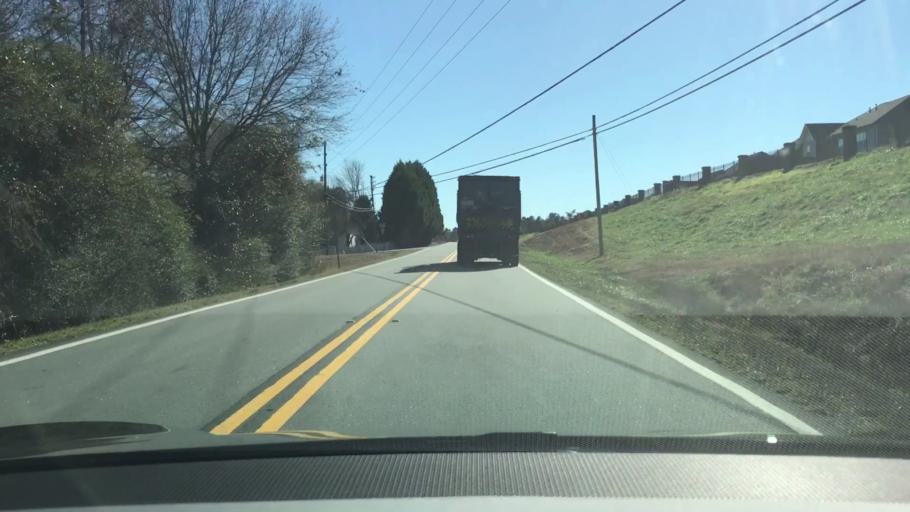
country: US
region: Georgia
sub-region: Barrow County
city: Auburn
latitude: 33.9279
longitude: -83.8284
